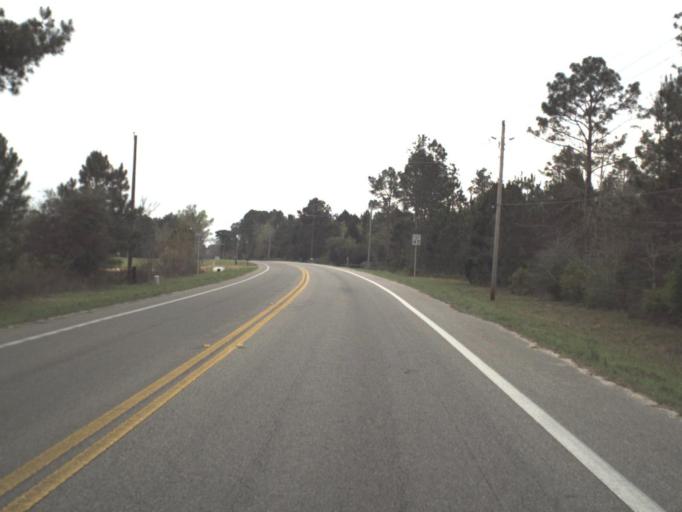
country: US
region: Florida
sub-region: Gulf County
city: Wewahitchka
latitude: 30.1407
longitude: -85.2103
